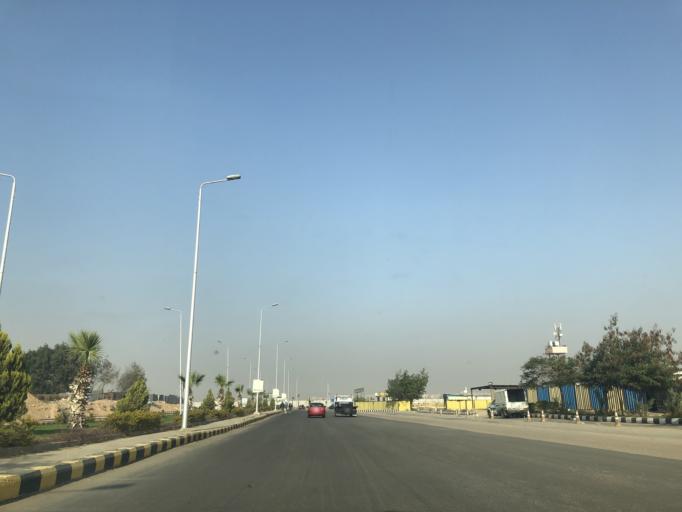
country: EG
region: Al Jizah
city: Madinat Sittah Uktubar
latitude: 29.9540
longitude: 31.0760
